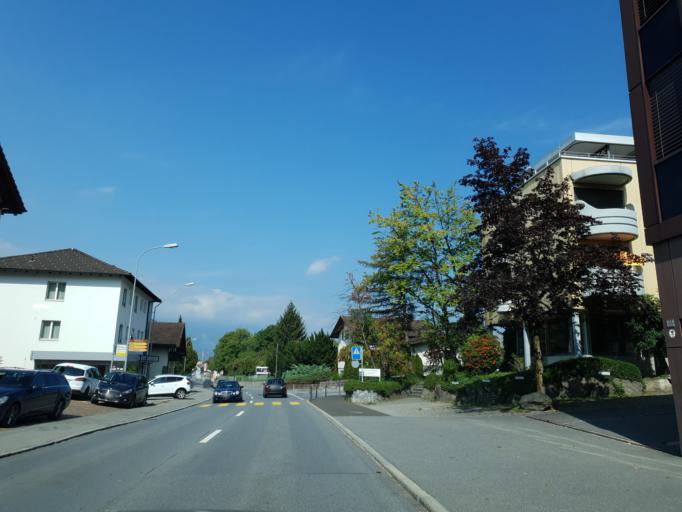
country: LI
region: Schaan
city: Schaan
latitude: 47.1577
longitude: 9.5096
